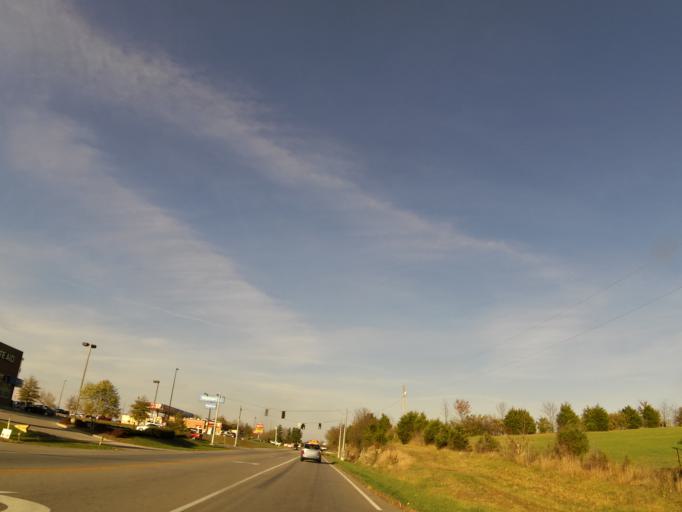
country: US
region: Kentucky
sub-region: Lincoln County
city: Stanford
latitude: 37.5464
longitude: -84.6476
